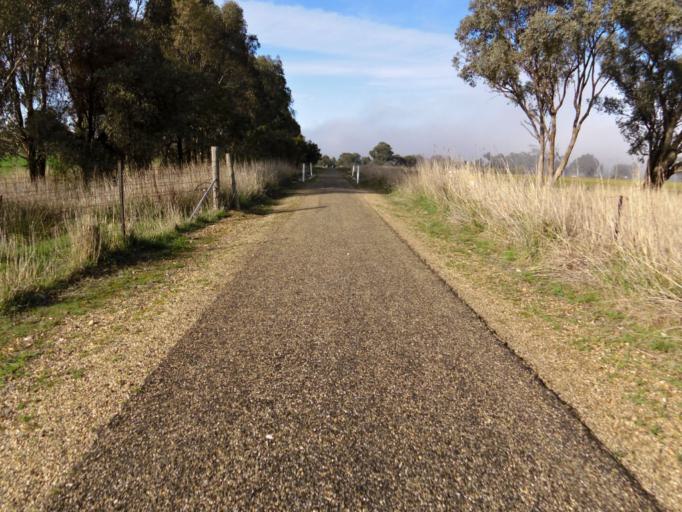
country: AU
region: Victoria
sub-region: Wangaratta
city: Wangaratta
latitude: -36.4375
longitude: 146.5509
